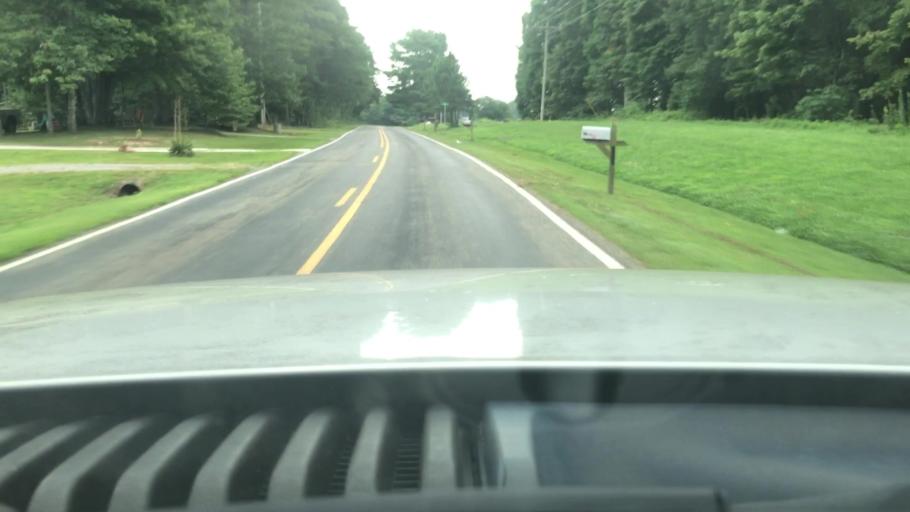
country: US
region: North Carolina
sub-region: Surry County
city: Dobson
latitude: 36.4062
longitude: -80.8114
